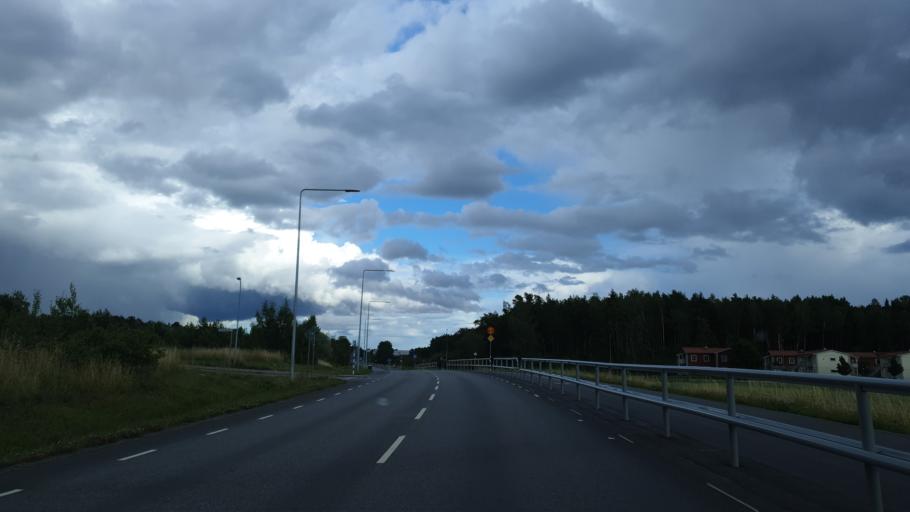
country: SE
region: Stockholm
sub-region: Jarfalla Kommun
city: Jakobsberg
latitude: 59.4241
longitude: 17.8018
